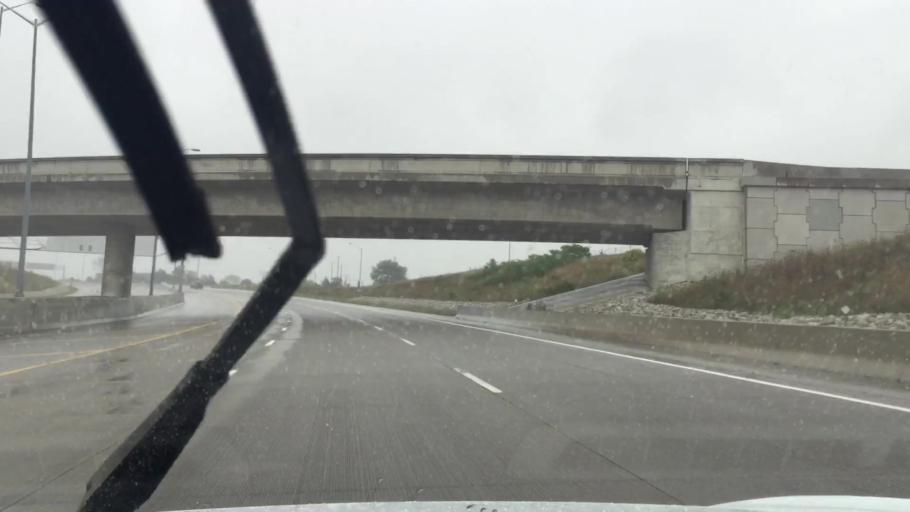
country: CA
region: Ontario
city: Windsor
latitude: 42.2330
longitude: -82.9911
